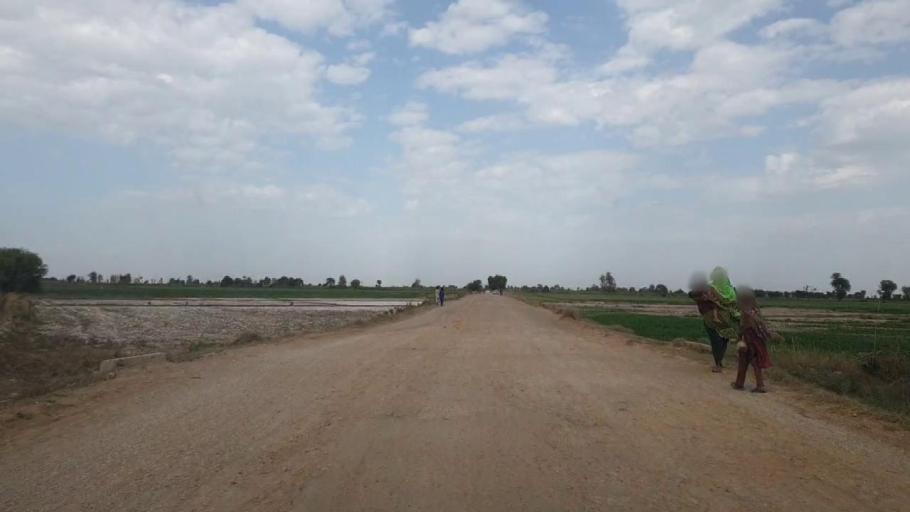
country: PK
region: Sindh
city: Hala
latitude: 25.9610
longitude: 68.4674
